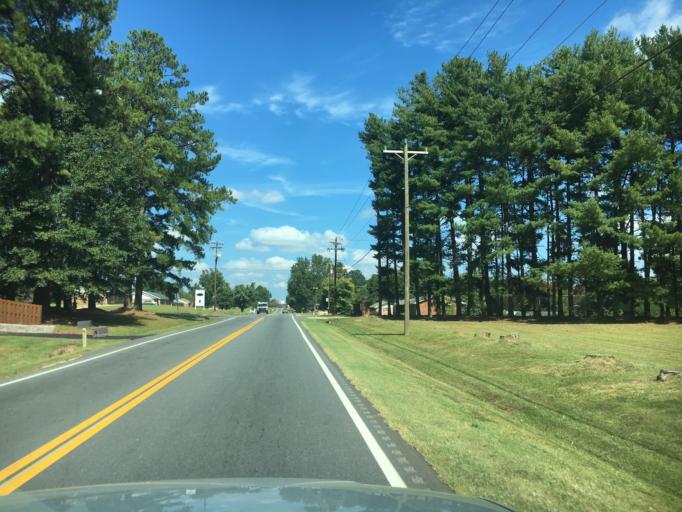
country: US
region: South Carolina
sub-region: Spartanburg County
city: Valley Falls
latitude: 35.0167
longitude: -81.9488
